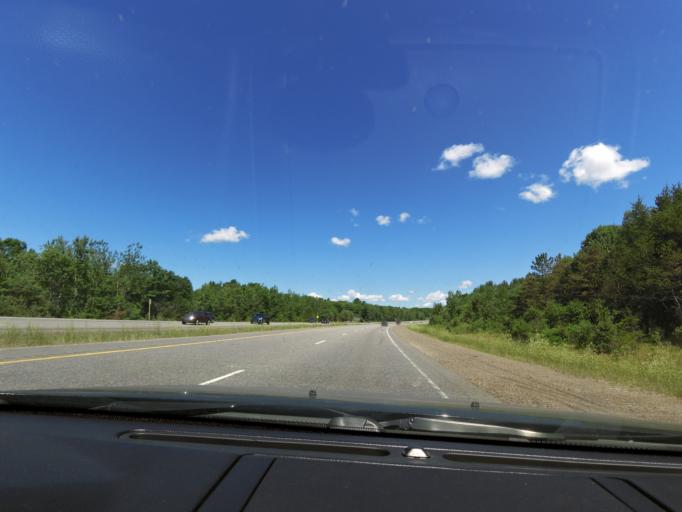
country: CA
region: Ontario
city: Bracebridge
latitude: 45.0610
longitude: -79.2959
